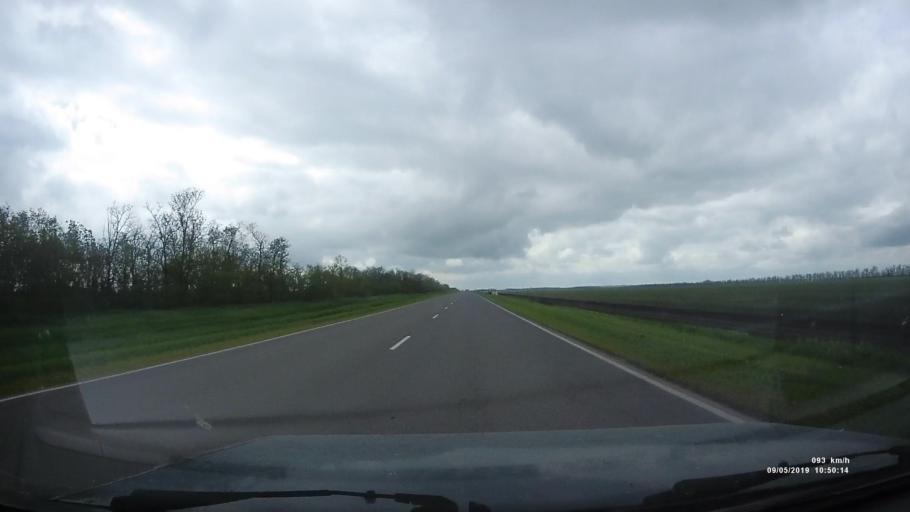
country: RU
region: Rostov
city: Peshkovo
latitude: 46.9315
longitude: 39.3554
